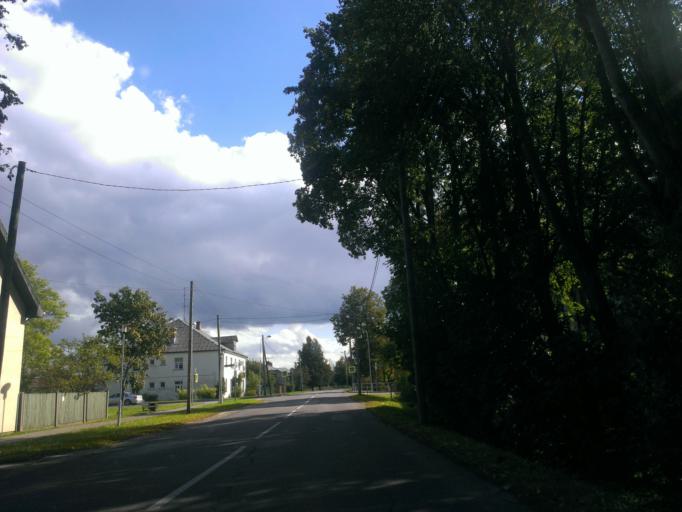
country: LV
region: Sigulda
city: Sigulda
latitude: 57.1491
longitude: 24.8556
